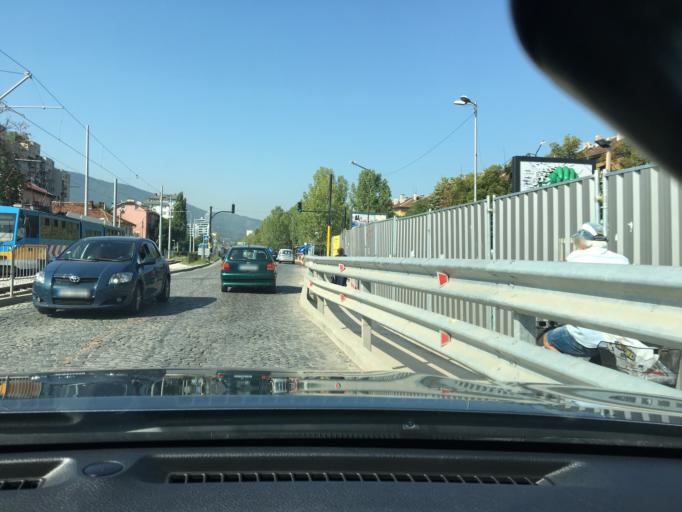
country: BG
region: Sofia-Capital
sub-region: Stolichna Obshtina
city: Sofia
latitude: 42.6789
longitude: 23.2850
